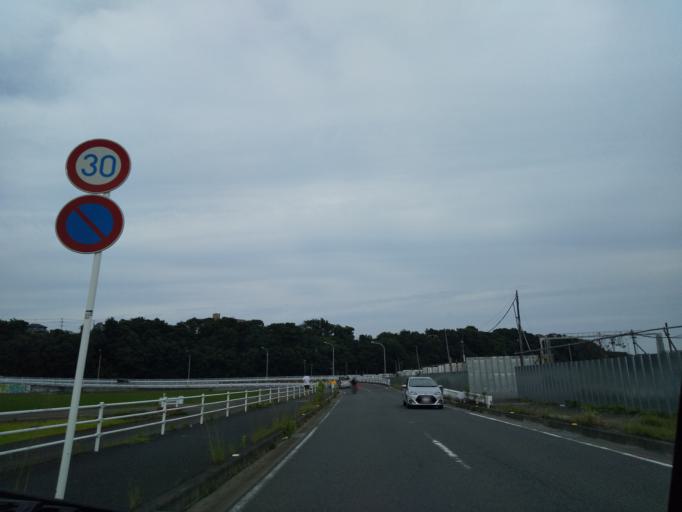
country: JP
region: Kanagawa
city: Zama
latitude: 35.4837
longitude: 139.3594
